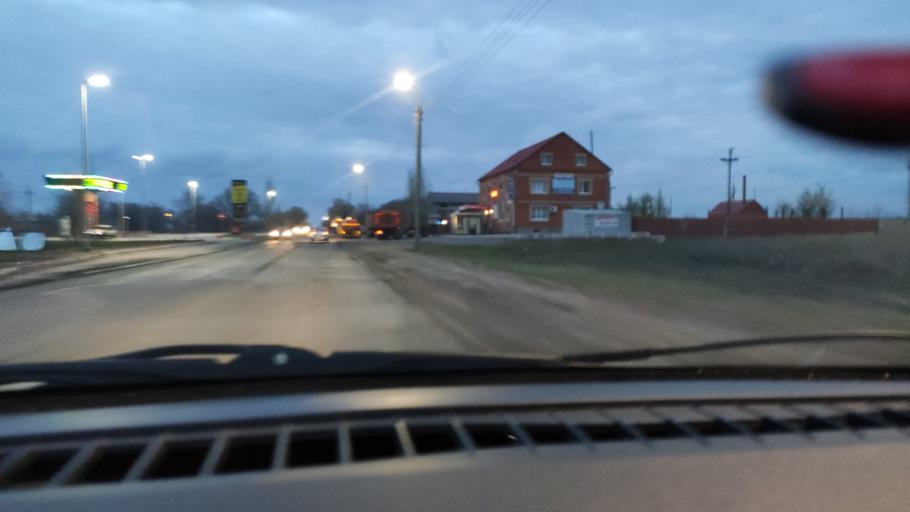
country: RU
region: Orenburg
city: Tatarskaya Kargala
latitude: 51.8699
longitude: 55.1436
